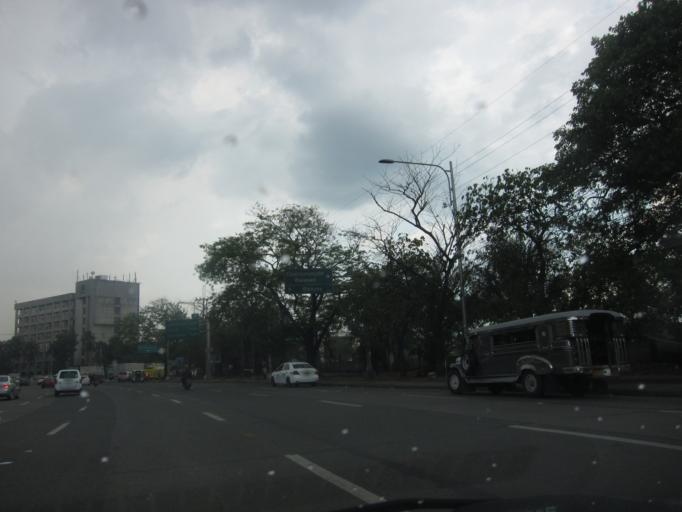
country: PH
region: Metro Manila
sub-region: Quezon City
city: Quezon City
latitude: 14.6515
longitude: 121.0520
